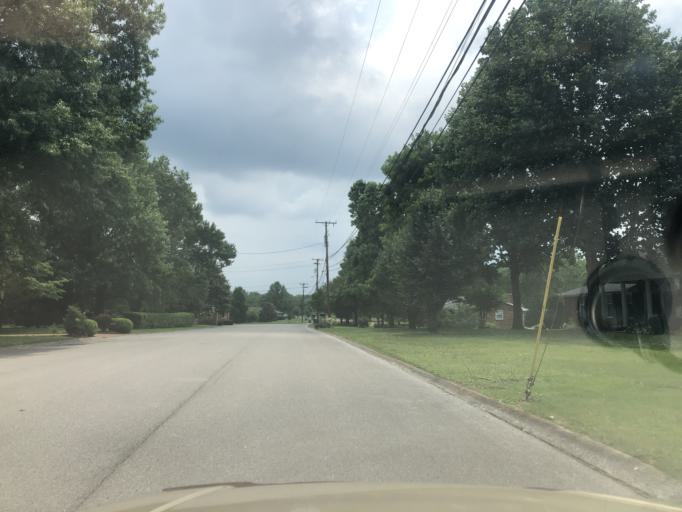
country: US
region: Tennessee
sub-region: Davidson County
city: Lakewood
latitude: 36.2364
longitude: -86.6164
